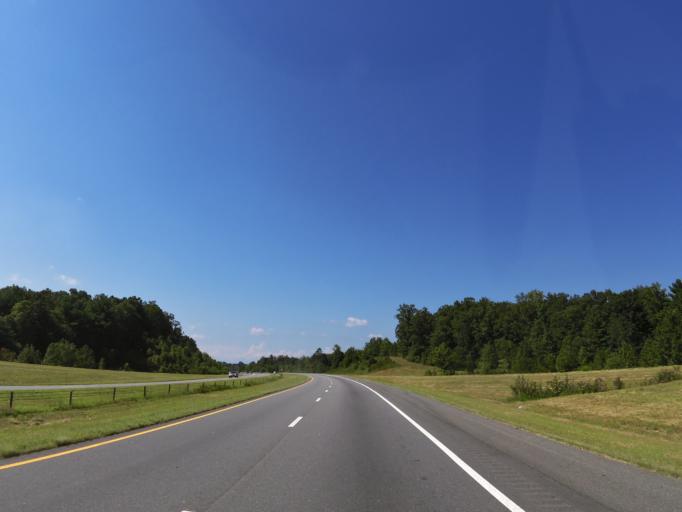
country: US
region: North Carolina
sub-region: Catawba County
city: Mountain View
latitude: 35.6812
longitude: -81.3407
